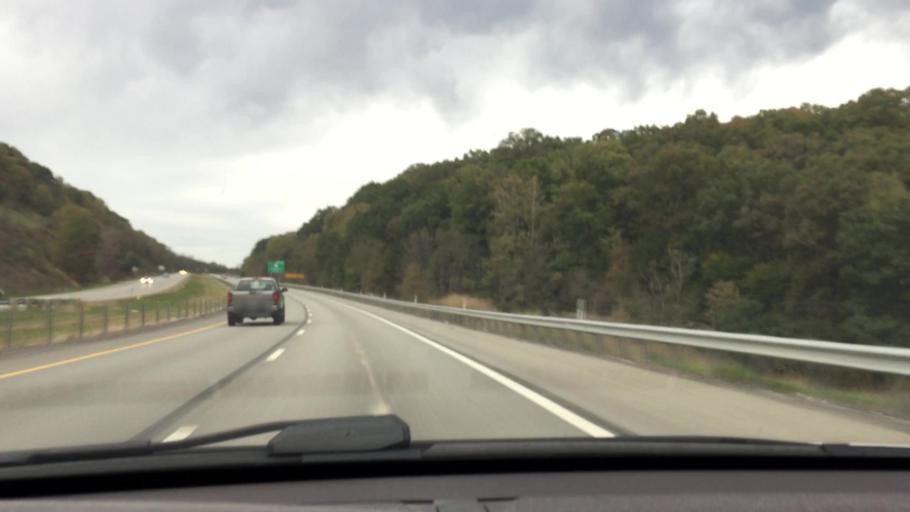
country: US
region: Pennsylvania
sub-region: Beaver County
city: Beaver Falls
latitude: 40.7261
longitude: -80.3680
